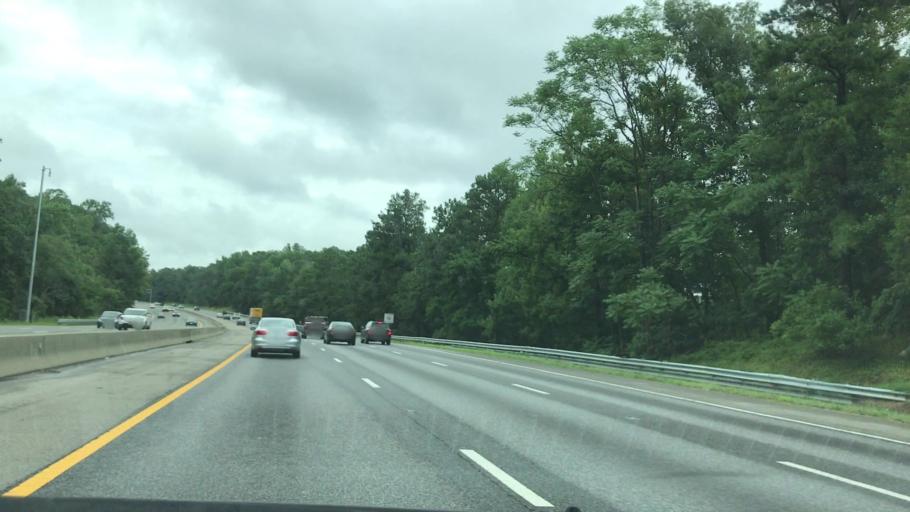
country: US
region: Virginia
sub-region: City of Colonial Heights
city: Colonial Heights
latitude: 37.2964
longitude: -77.3908
